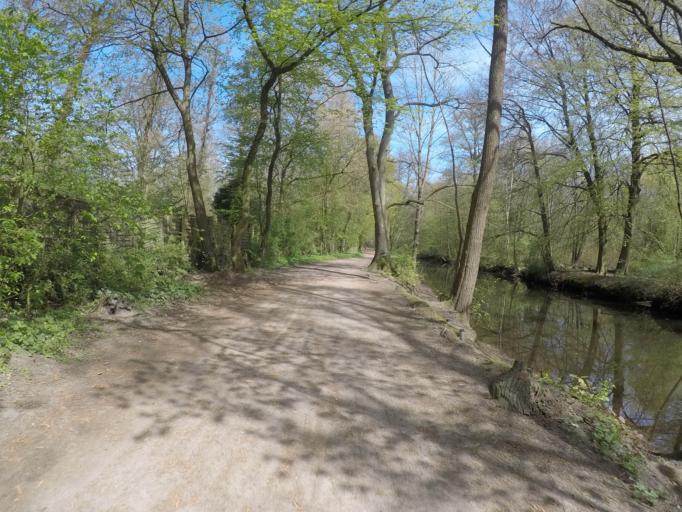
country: DE
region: Hamburg
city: Hummelsbuettel
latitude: 53.6369
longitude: 10.0537
